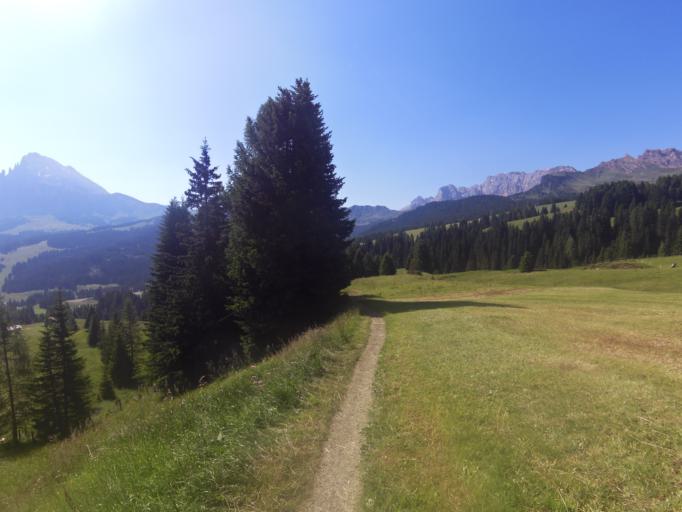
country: IT
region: Trentino-Alto Adige
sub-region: Bolzano
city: Ortisei
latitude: 46.5340
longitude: 11.6560
